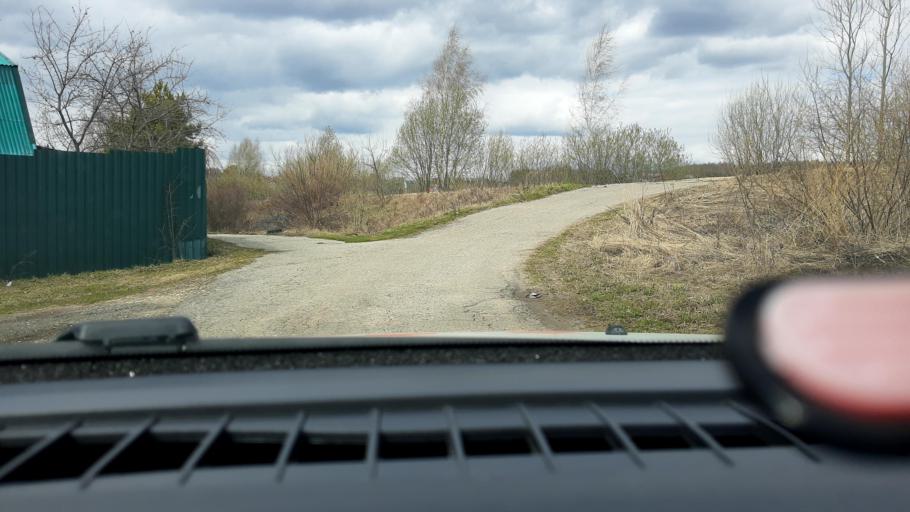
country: RU
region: Nizjnij Novgorod
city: Babino
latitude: 56.1708
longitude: 43.6753
